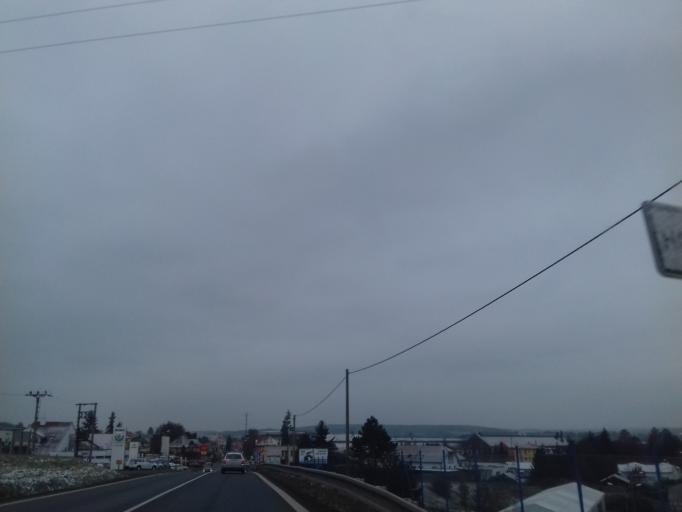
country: CZ
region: Plzensky
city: Holysov
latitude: 49.5986
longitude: 13.1067
